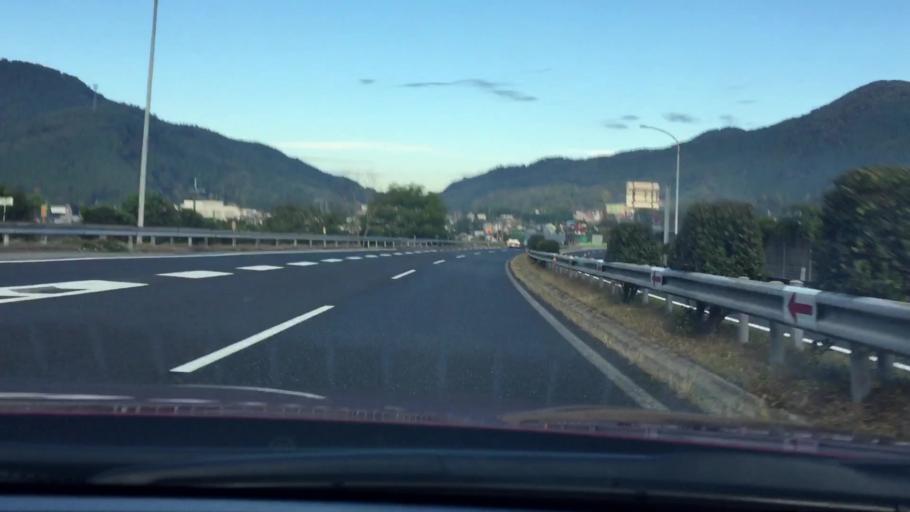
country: JP
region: Hyogo
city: Yamazakicho-nakabirose
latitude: 34.9851
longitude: 134.6011
